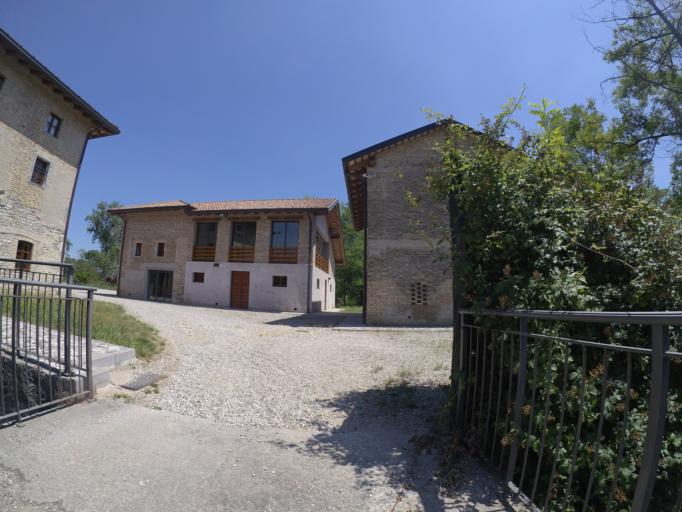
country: IT
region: Friuli Venezia Giulia
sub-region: Provincia di Udine
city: Bertiolo
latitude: 45.9151
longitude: 13.0767
